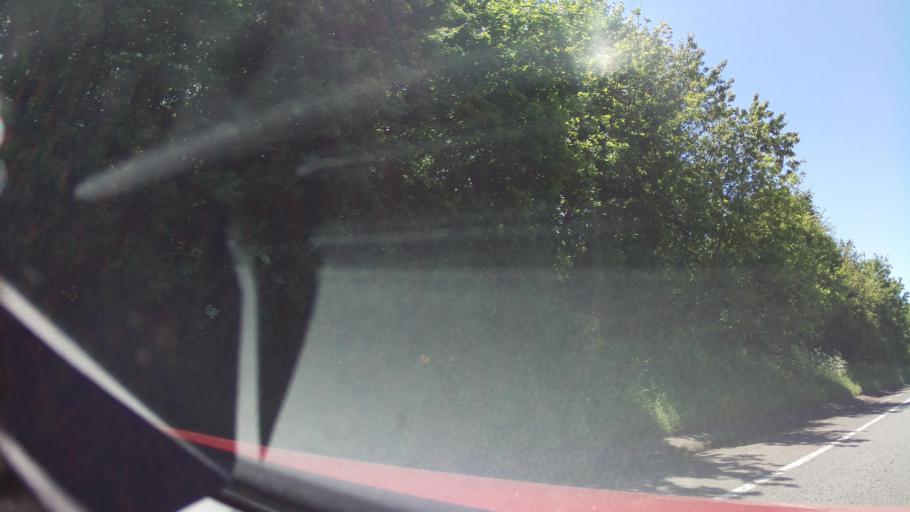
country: GB
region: England
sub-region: Devon
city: Honiton
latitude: 50.7869
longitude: -3.2338
